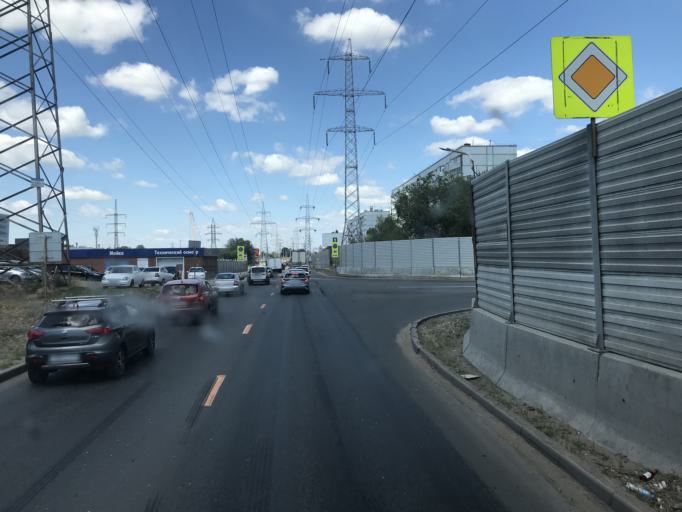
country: RU
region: Samara
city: Zhigulevsk
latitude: 53.4747
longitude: 49.5120
